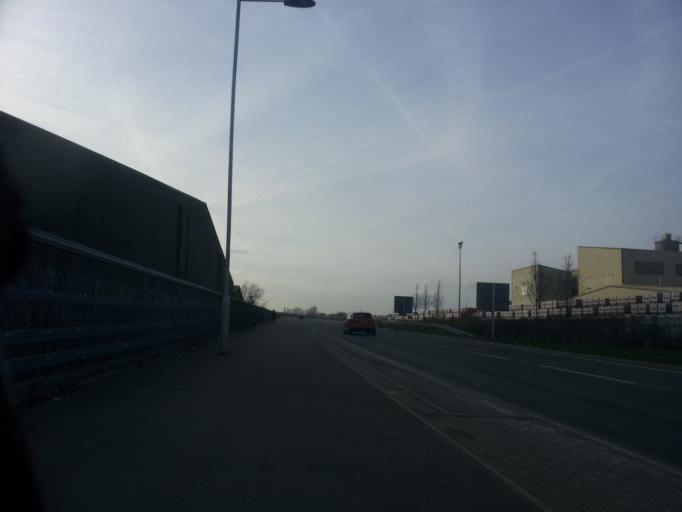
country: GB
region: England
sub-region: Kent
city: Sittingbourne
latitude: 51.3521
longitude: 0.7596
